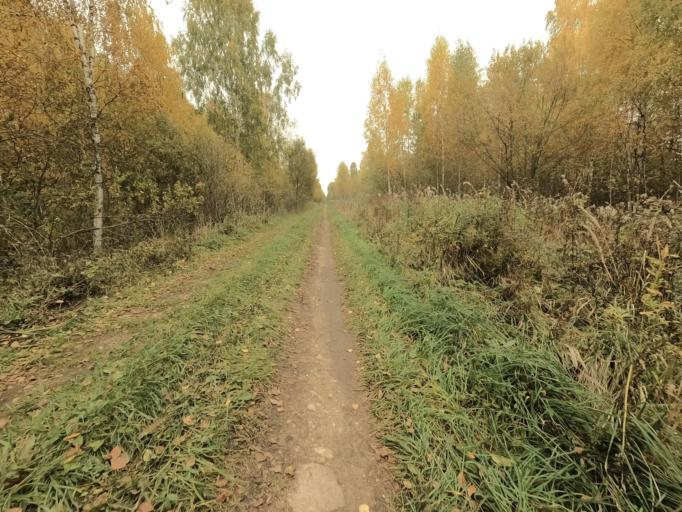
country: RU
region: Novgorod
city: Pankovka
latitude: 58.8874
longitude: 30.9476
